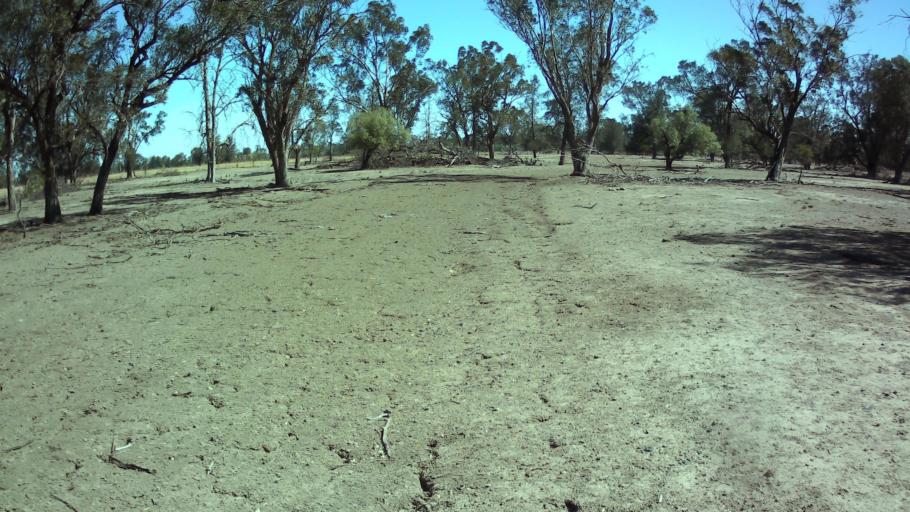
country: AU
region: New South Wales
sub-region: Bland
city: West Wyalong
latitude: -33.7645
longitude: 147.6584
